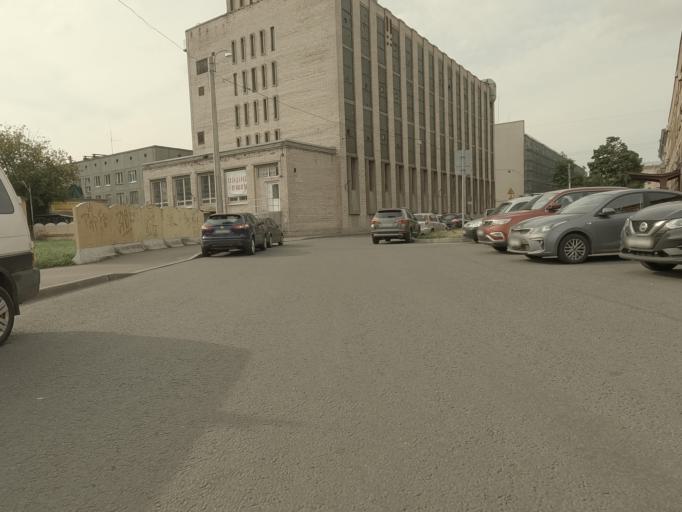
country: RU
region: St.-Petersburg
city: Admiralteisky
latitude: 59.8937
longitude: 30.2809
